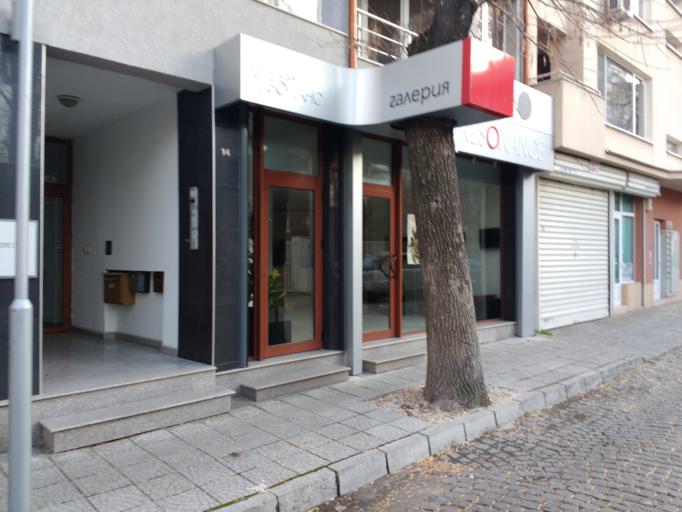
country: BG
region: Plovdiv
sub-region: Obshtina Plovdiv
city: Plovdiv
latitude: 42.1430
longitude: 24.7527
